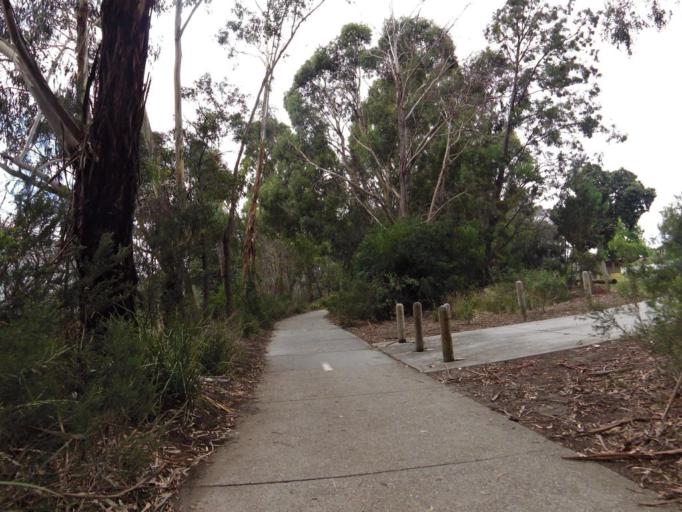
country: AU
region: Victoria
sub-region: Monash
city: Ashwood
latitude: -37.8555
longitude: 145.1062
